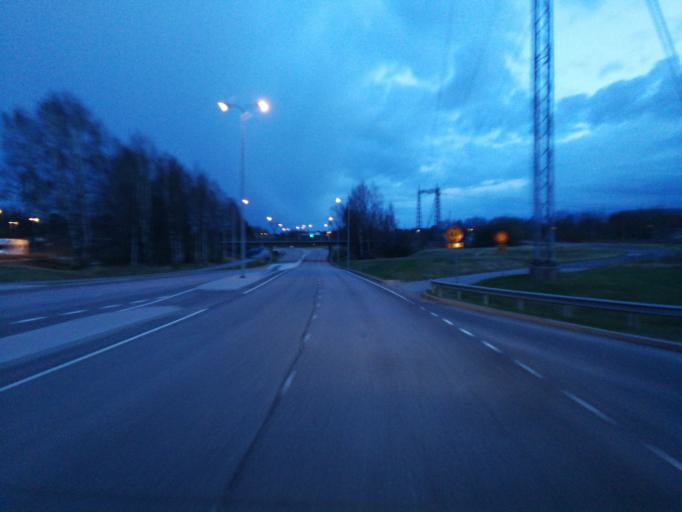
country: FI
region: Varsinais-Suomi
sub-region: Turku
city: Raisio
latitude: 60.4597
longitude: 22.1959
